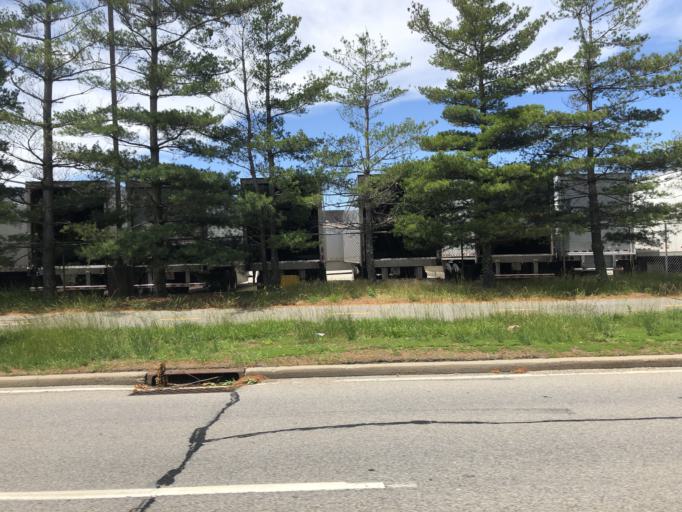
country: US
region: New York
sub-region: Nassau County
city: East Garden City
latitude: 40.7258
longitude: -73.6046
